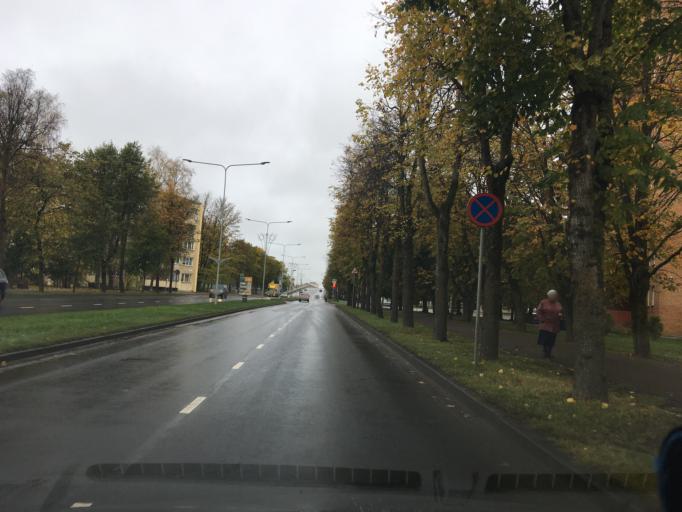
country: EE
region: Ida-Virumaa
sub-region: Narva linn
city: Narva
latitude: 59.3676
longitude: 28.1866
